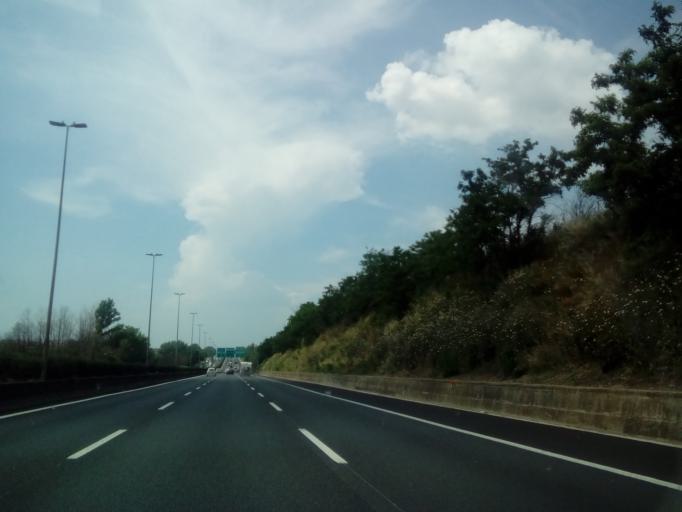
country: IT
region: Latium
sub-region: Citta metropolitana di Roma Capitale
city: Colle Verde
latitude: 41.9667
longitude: 12.5627
